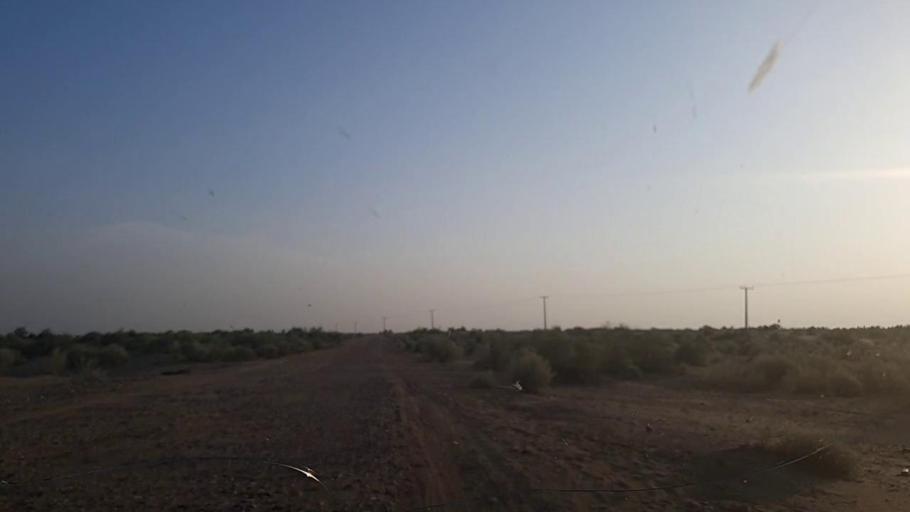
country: PK
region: Sindh
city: Khanpur
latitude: 27.6442
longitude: 69.4580
